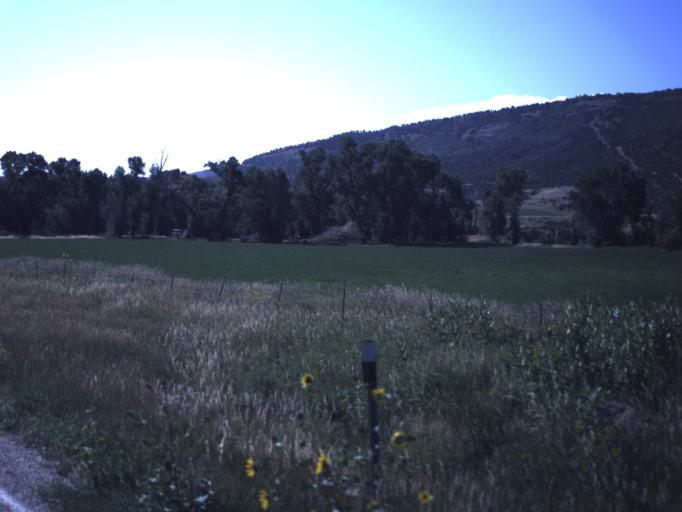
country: US
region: Utah
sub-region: Duchesne County
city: Duchesne
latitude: 40.3885
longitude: -110.7471
